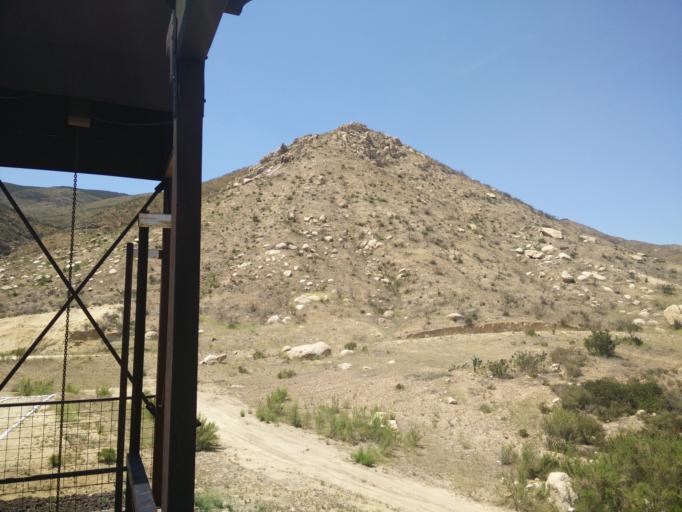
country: MX
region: Baja California
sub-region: Ensenada
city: Rancho Verde
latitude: 32.0513
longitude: -116.6687
